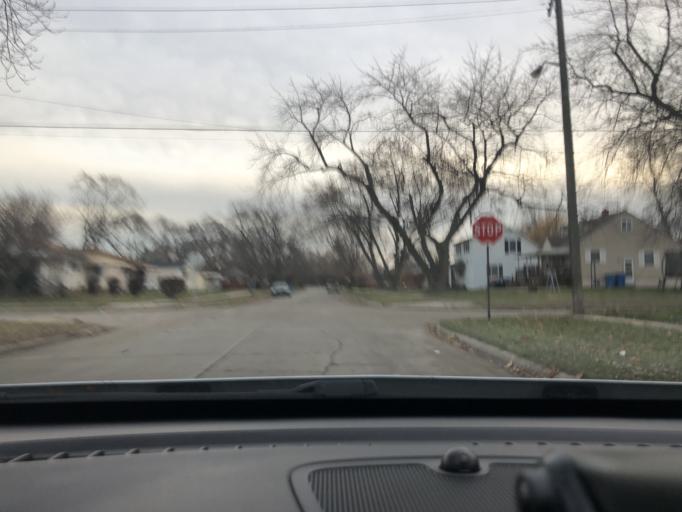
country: US
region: Michigan
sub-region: Wayne County
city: Allen Park
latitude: 42.2757
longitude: -83.2229
